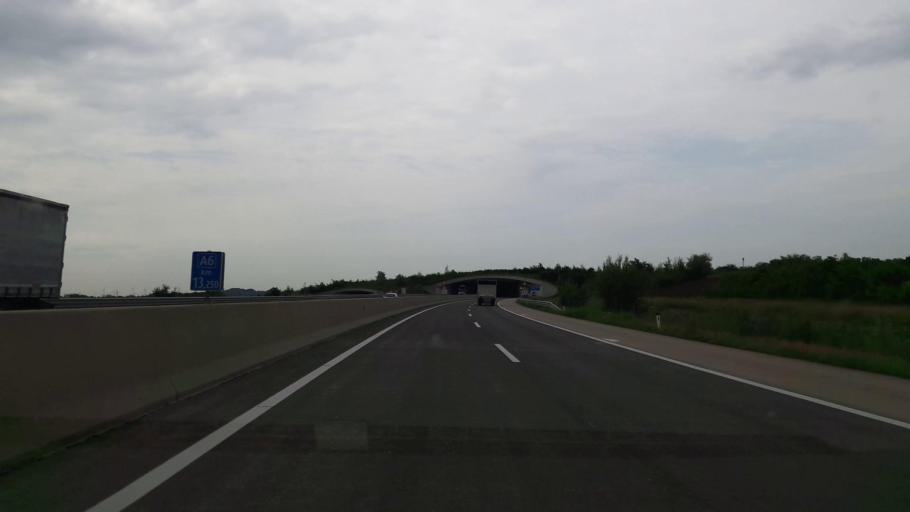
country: AT
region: Burgenland
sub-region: Politischer Bezirk Neusiedl am See
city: Gattendorf
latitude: 48.0420
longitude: 16.9916
